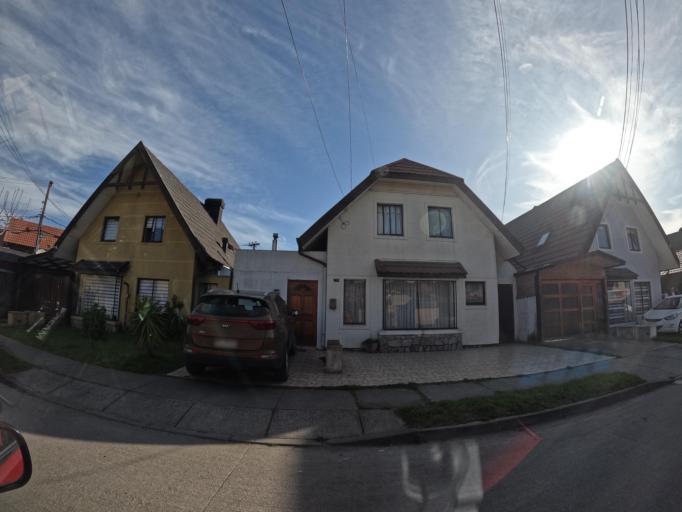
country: CL
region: Biobio
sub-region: Provincia de Concepcion
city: Talcahuano
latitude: -36.7709
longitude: -73.0772
